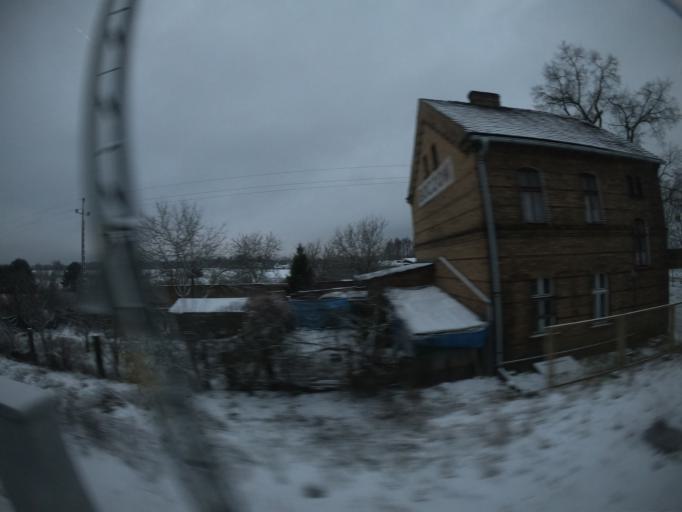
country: PL
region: Lubusz
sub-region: Powiat slubicki
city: Rzepin
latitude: 52.3269
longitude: 14.9501
